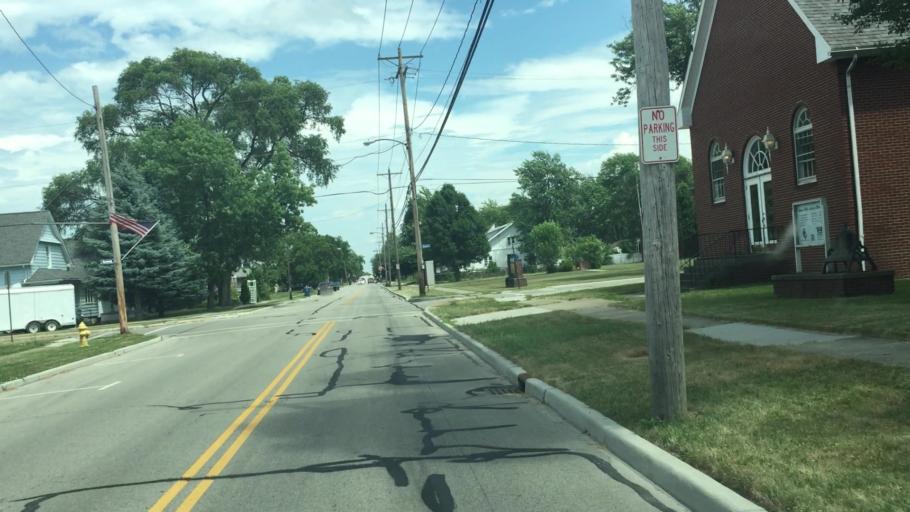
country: US
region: Ohio
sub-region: Wood County
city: Walbridge
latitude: 41.5878
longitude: -83.4917
